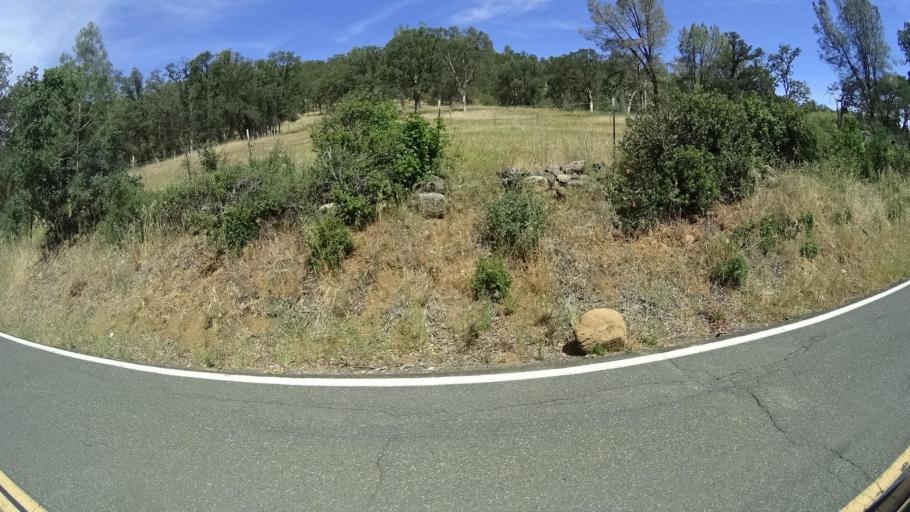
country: US
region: California
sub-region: Lake County
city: Lower Lake
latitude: 38.8968
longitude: -122.6487
